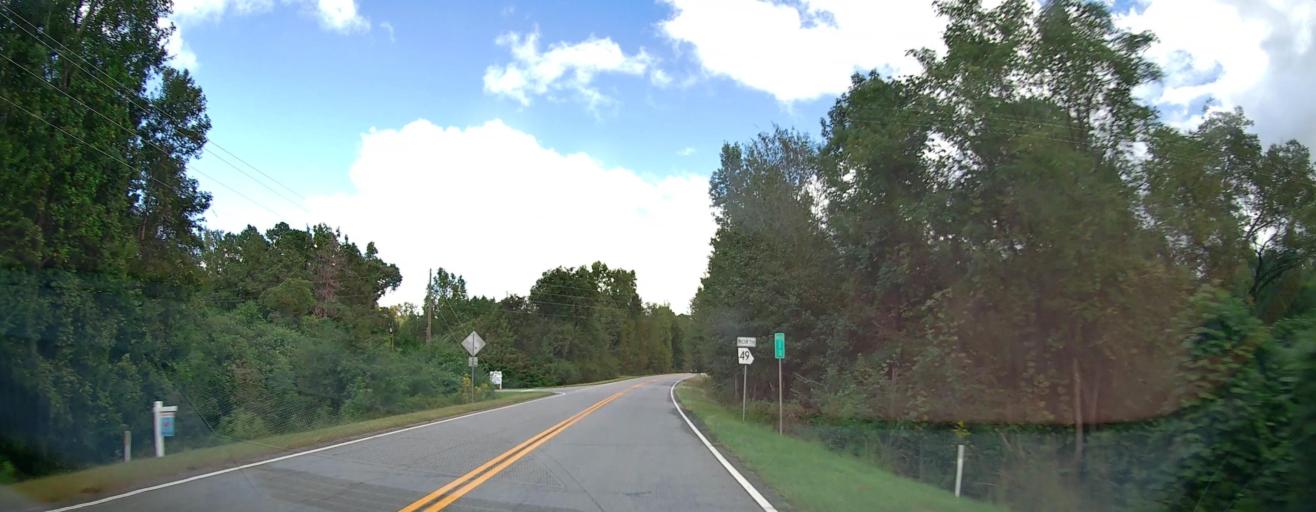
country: US
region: Georgia
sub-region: Jones County
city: Gray
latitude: 32.9820
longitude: -83.4166
